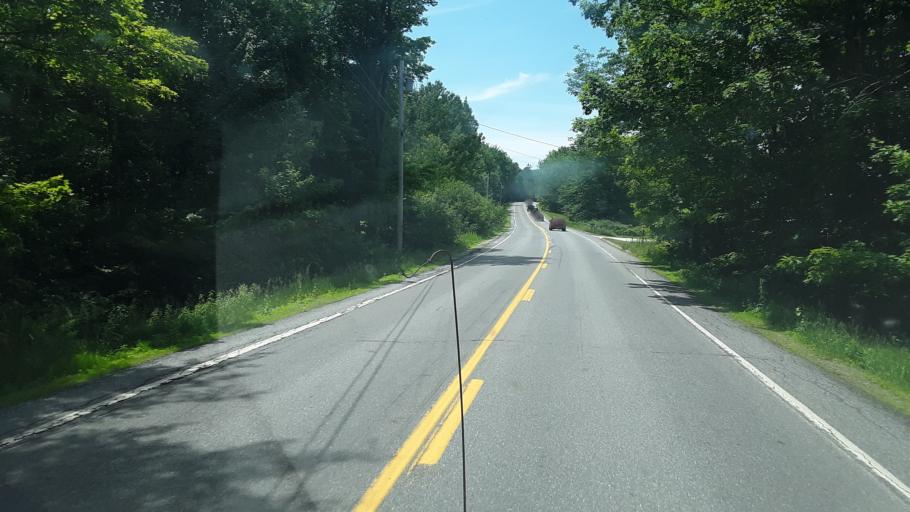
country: US
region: Maine
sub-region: Hancock County
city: Bucksport
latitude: 44.5638
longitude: -68.8388
